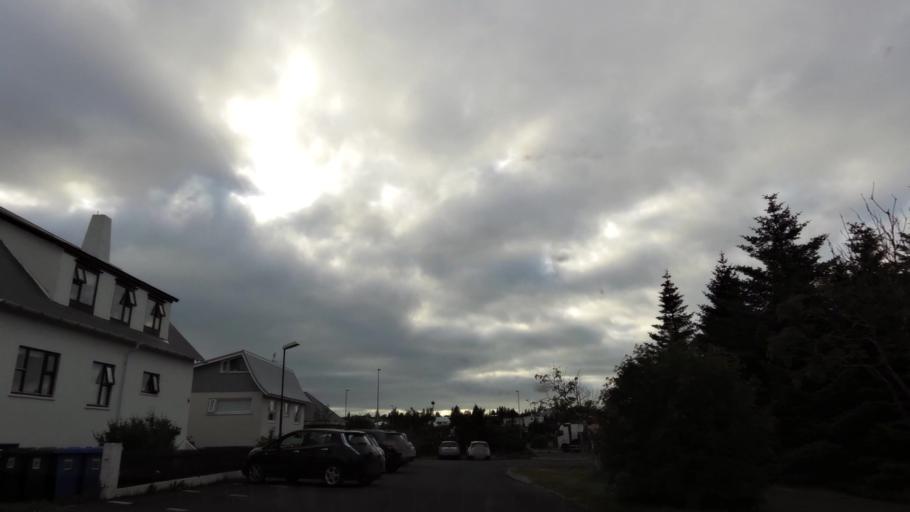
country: IS
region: Capital Region
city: Hafnarfjoerdur
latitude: 64.0664
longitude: -21.9419
